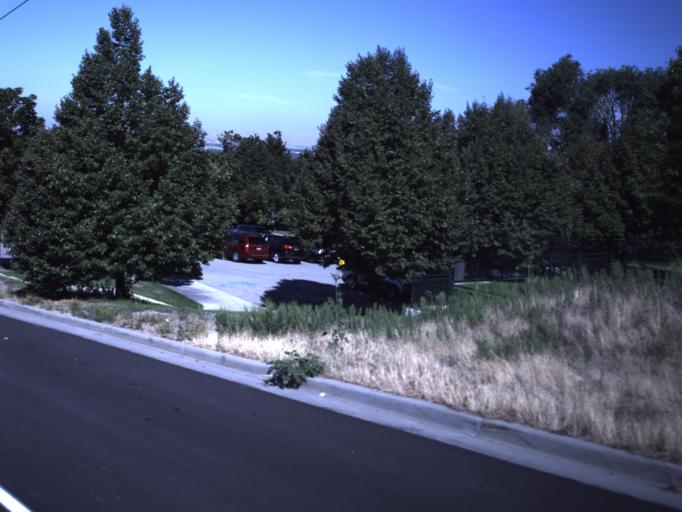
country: US
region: Utah
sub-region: Salt Lake County
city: Mount Olympus
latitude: 40.6749
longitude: -111.8044
